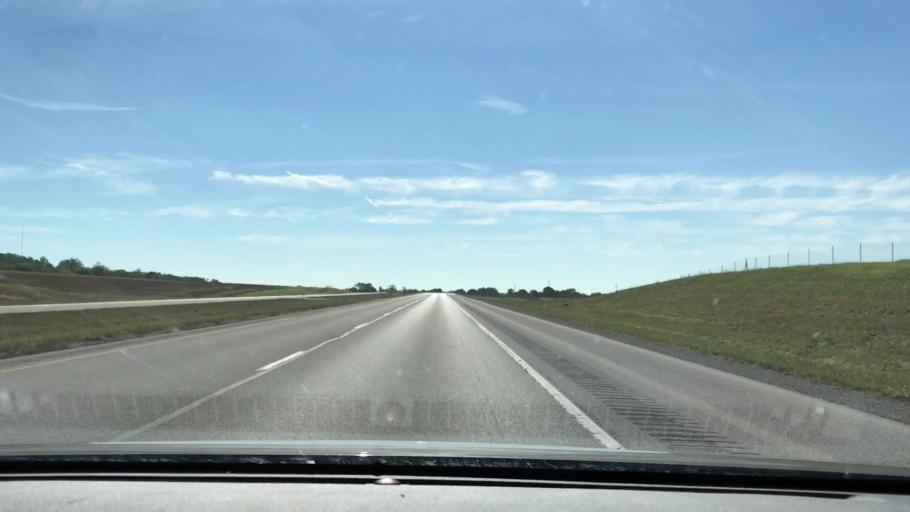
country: US
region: Kentucky
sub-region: Todd County
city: Elkton
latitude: 36.8178
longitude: -87.1429
